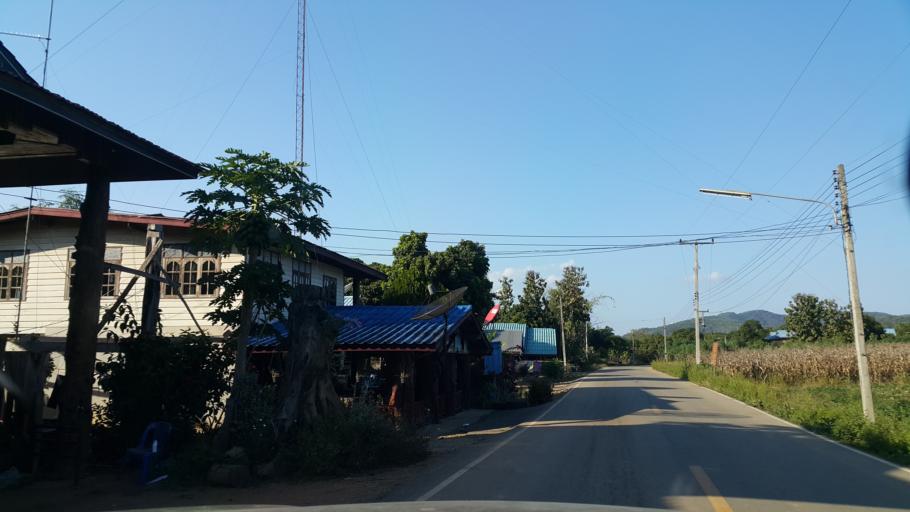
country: TH
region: Sukhothai
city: Thung Saliam
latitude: 17.4114
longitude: 99.5134
